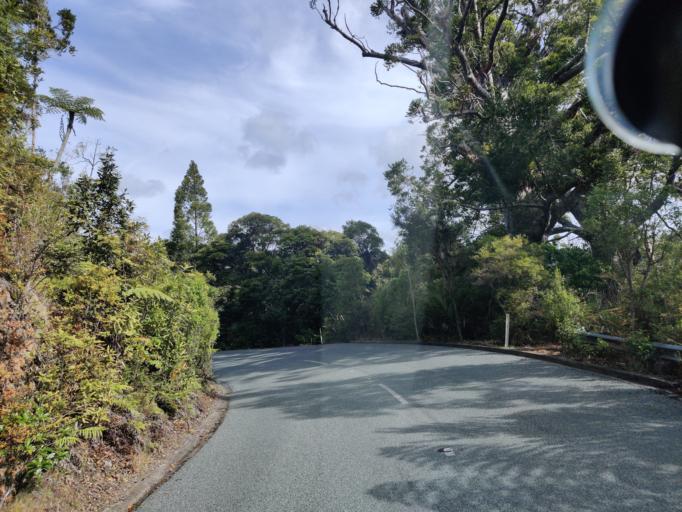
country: NZ
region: Northland
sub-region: Kaipara District
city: Dargaville
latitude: -35.6492
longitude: 173.5606
